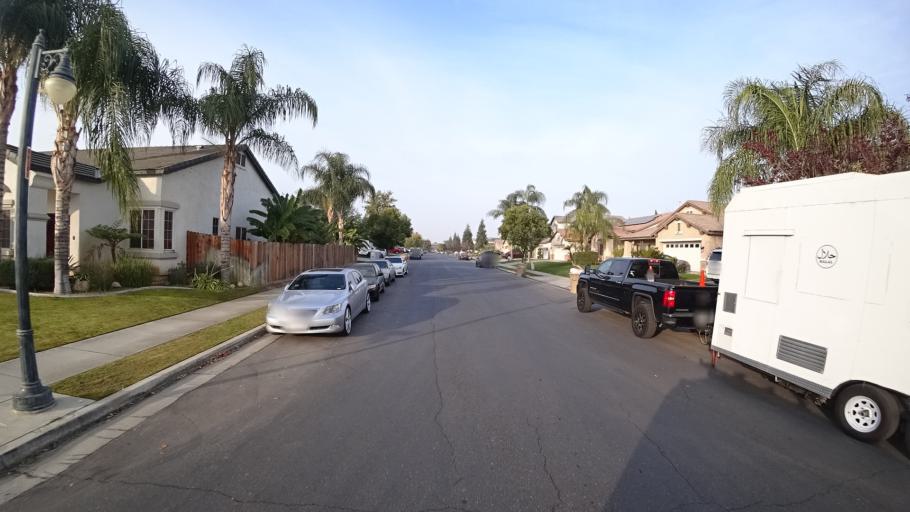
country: US
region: California
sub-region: Kern County
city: Greenacres
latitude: 35.4246
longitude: -119.1235
